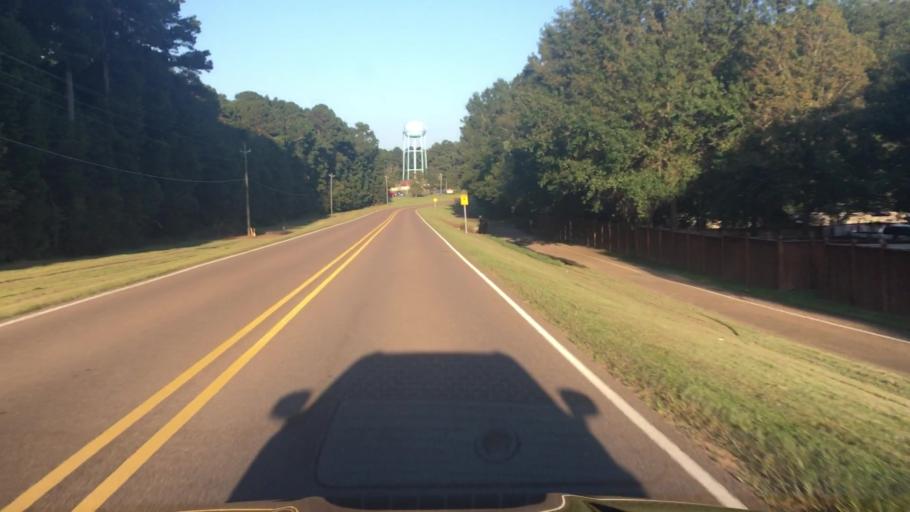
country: US
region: Mississippi
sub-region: Madison County
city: Madison
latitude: 32.4060
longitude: -90.0016
